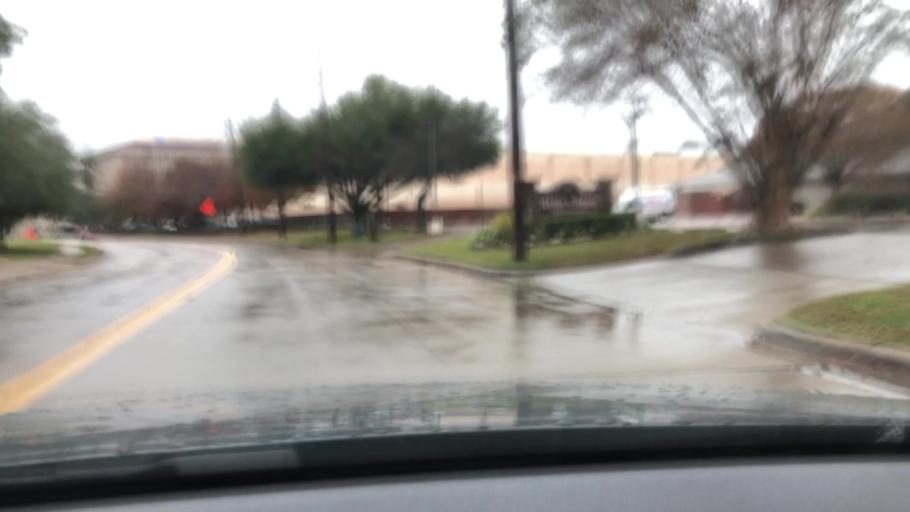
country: US
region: Texas
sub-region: Harris County
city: Bunker Hill Village
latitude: 29.7818
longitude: -95.5565
